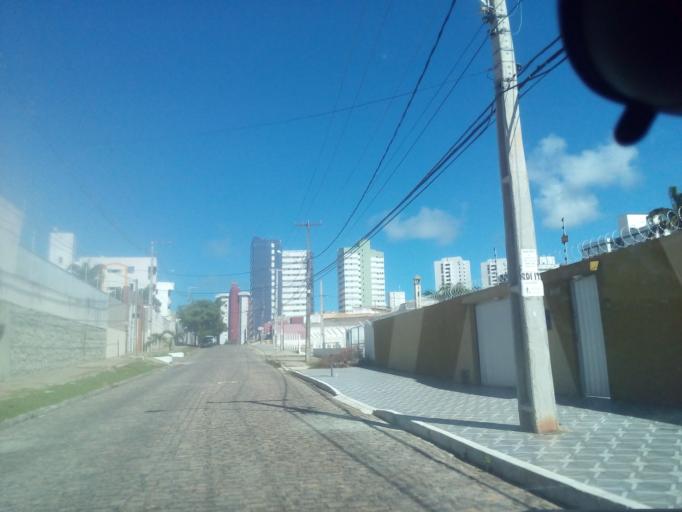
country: BR
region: Rio Grande do Norte
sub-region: Natal
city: Natal
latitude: -5.8527
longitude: -35.2073
